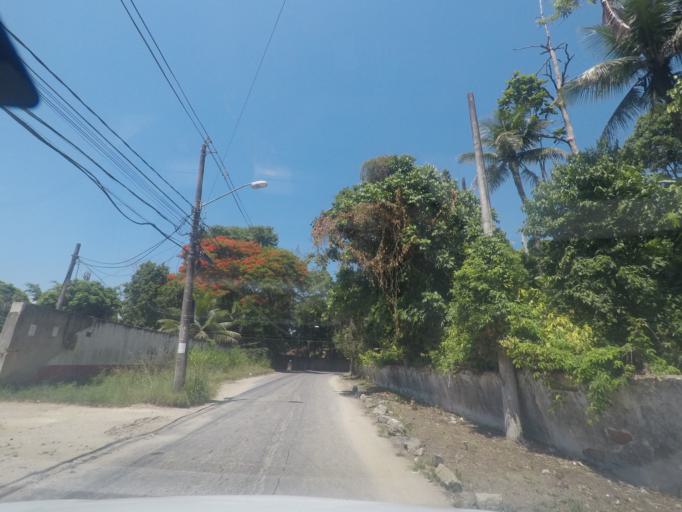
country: BR
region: Rio de Janeiro
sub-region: Nilopolis
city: Nilopolis
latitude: -22.9800
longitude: -43.4587
